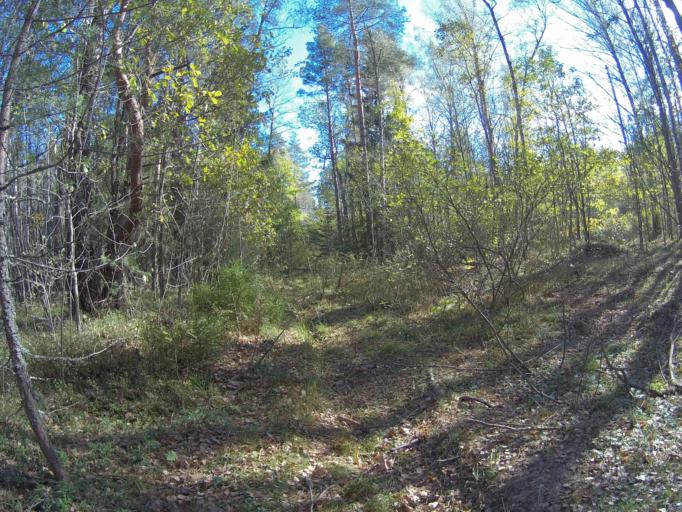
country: RU
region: Vladimir
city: Golovino
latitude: 56.0187
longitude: 40.4799
